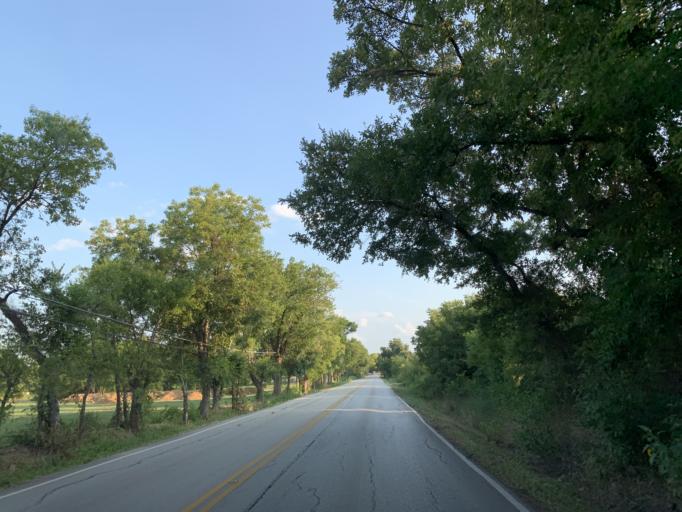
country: US
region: Texas
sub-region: Tarrant County
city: Hurst
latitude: 32.7776
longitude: -97.1750
